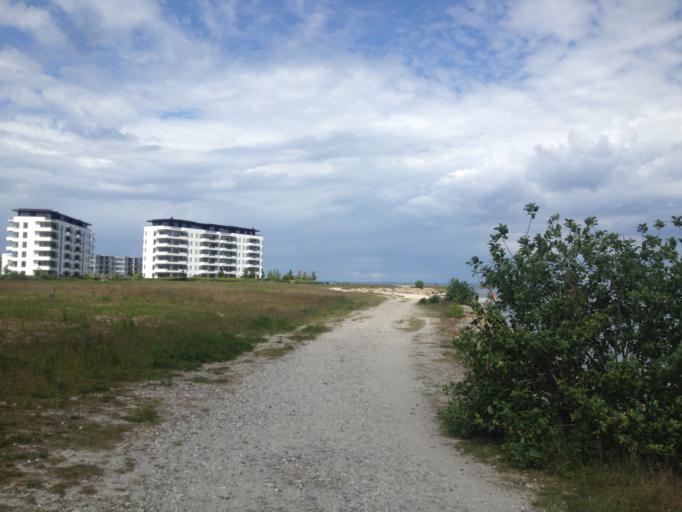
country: DK
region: Capital Region
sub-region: Gentofte Kommune
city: Charlottenlund
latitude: 55.7229
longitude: 12.5850
